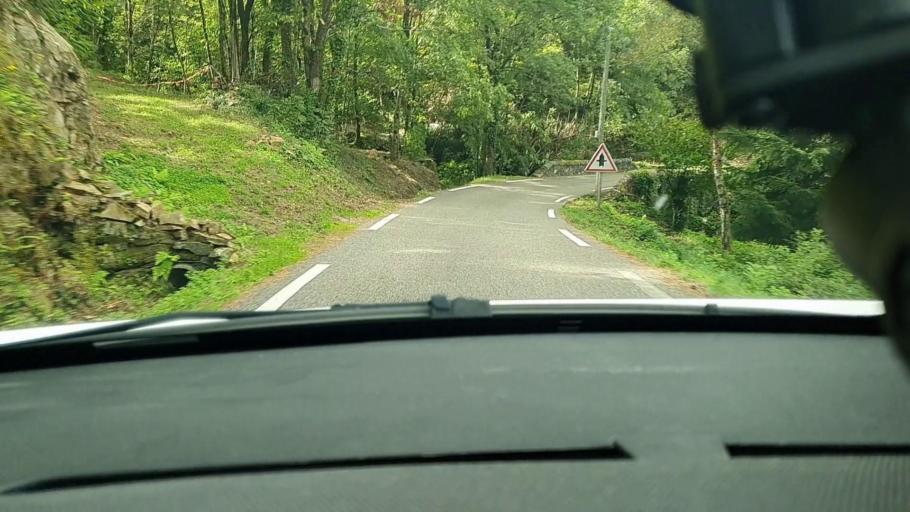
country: FR
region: Languedoc-Roussillon
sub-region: Departement du Gard
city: Besseges
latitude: 44.3006
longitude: 4.0188
